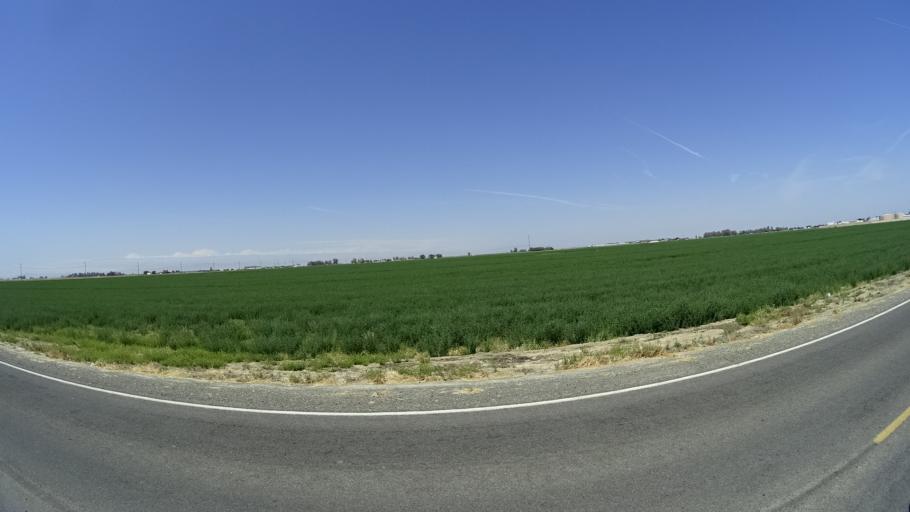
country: US
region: California
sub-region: Kings County
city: Stratford
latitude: 36.2286
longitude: -119.7625
